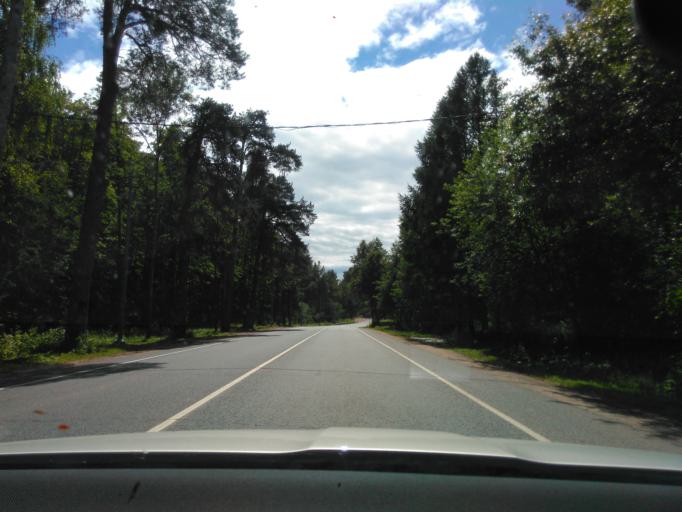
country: RU
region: Moskovskaya
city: Shevlyakovo
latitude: 56.3875
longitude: 36.8613
